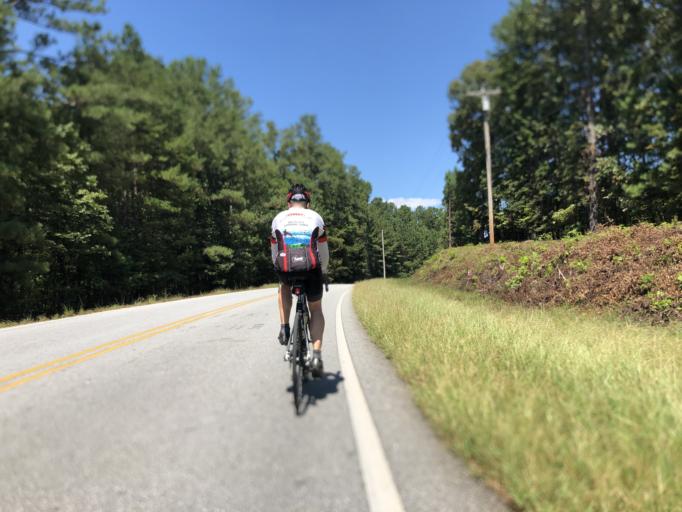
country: US
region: Georgia
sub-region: Fulton County
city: Chattahoochee Hills
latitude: 33.4884
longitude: -84.8002
